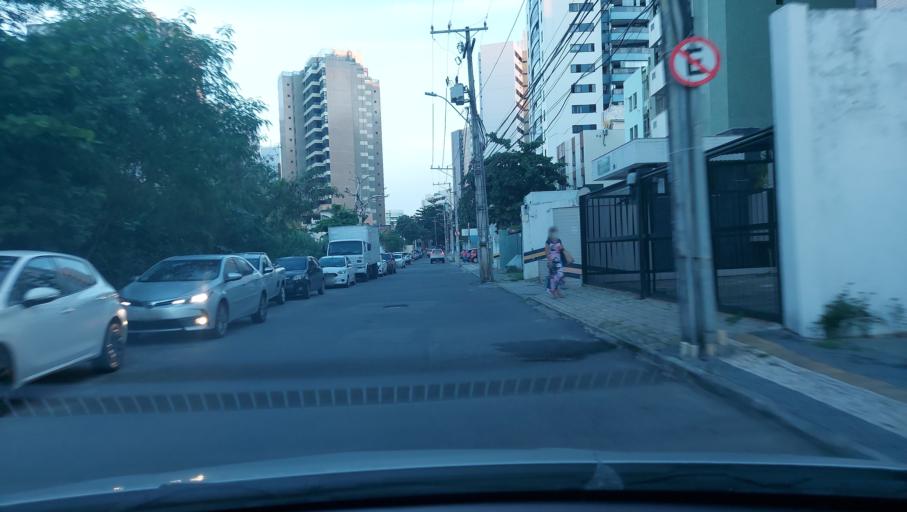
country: BR
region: Bahia
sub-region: Salvador
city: Salvador
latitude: -12.9854
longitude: -38.4395
